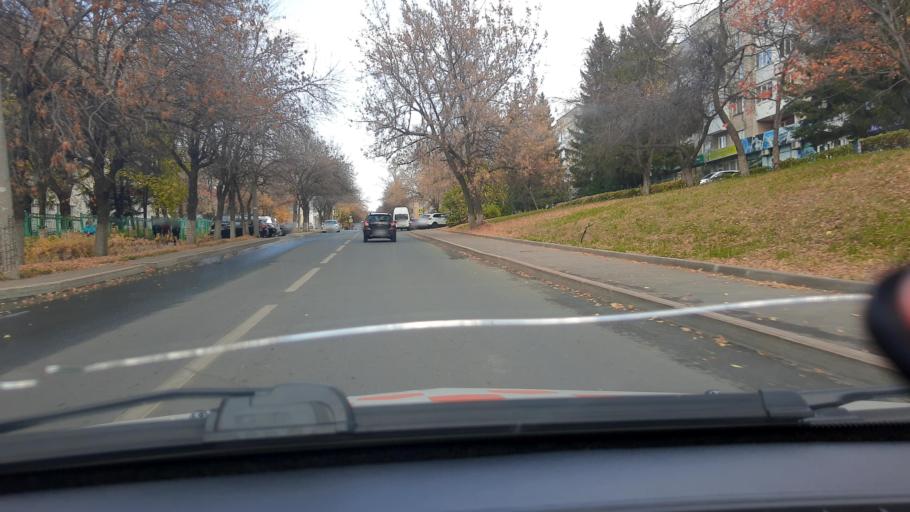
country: RU
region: Bashkortostan
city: Ufa
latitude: 54.8148
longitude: 56.0662
